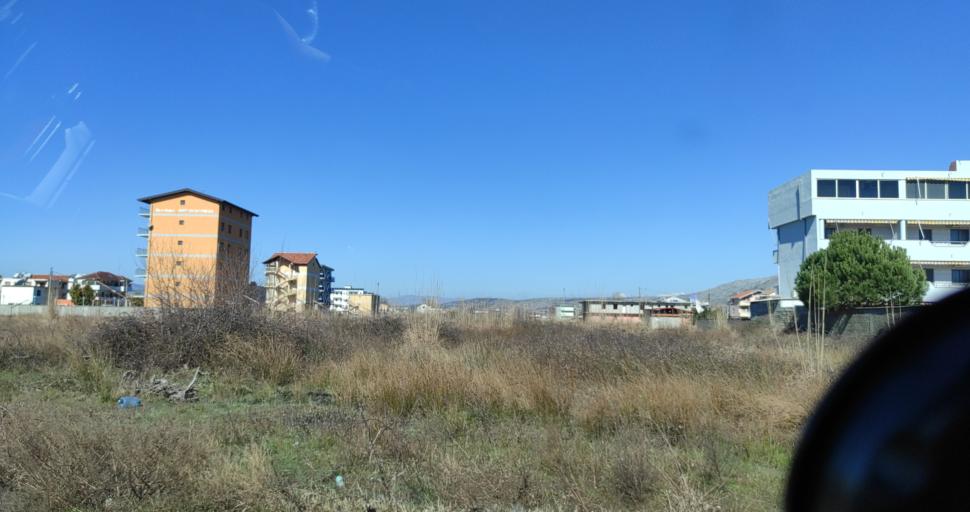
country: AL
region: Shkoder
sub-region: Rrethi i Shkodres
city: Velipoje
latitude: 41.8627
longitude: 19.4344
